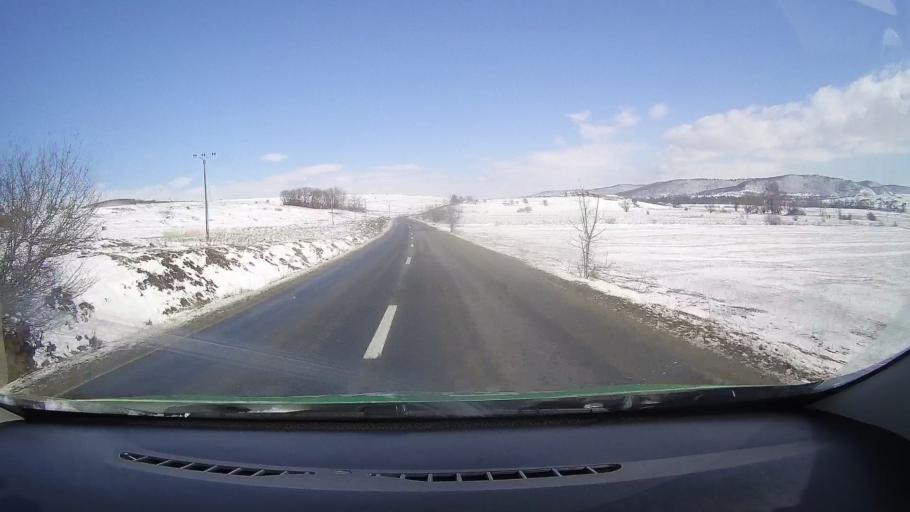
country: RO
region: Sibiu
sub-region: Comuna Rosia
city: Rosia
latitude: 45.8134
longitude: 24.3638
